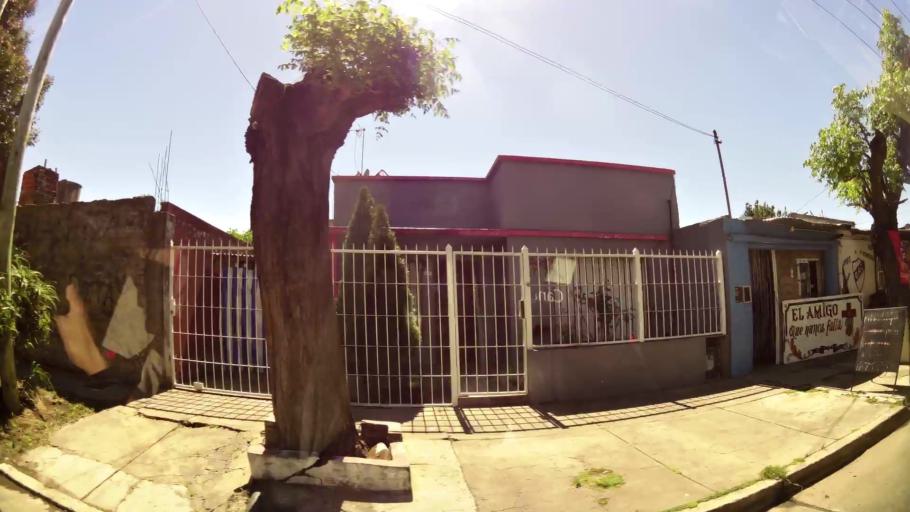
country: AR
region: Buenos Aires
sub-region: Partido de Quilmes
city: Quilmes
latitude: -34.7085
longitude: -58.2644
